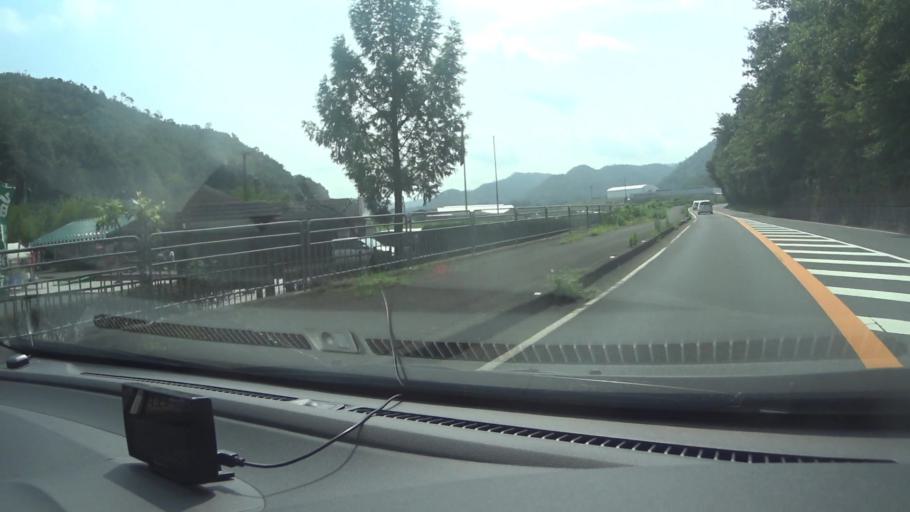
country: JP
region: Kyoto
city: Ayabe
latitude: 35.1676
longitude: 135.3605
